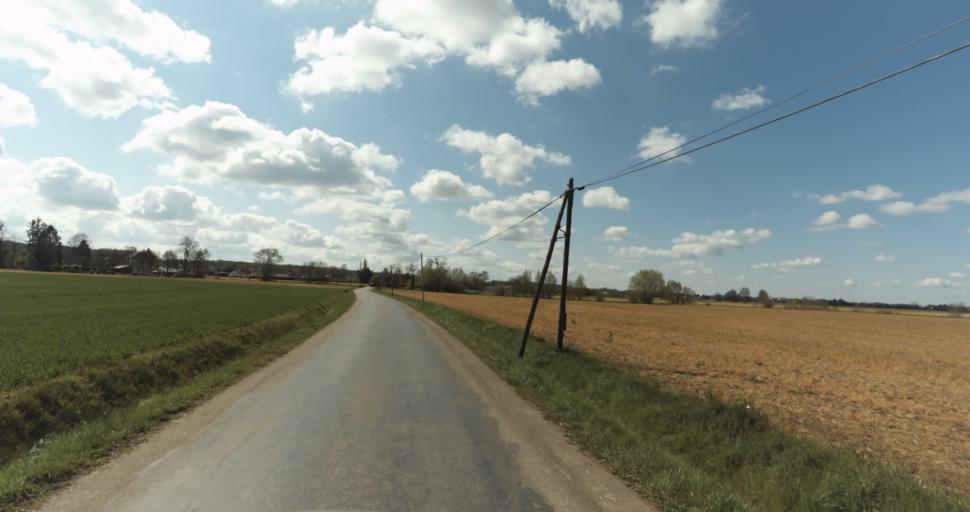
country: FR
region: Bourgogne
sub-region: Departement de la Cote-d'Or
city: Auxonne
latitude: 47.2048
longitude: 5.4235
